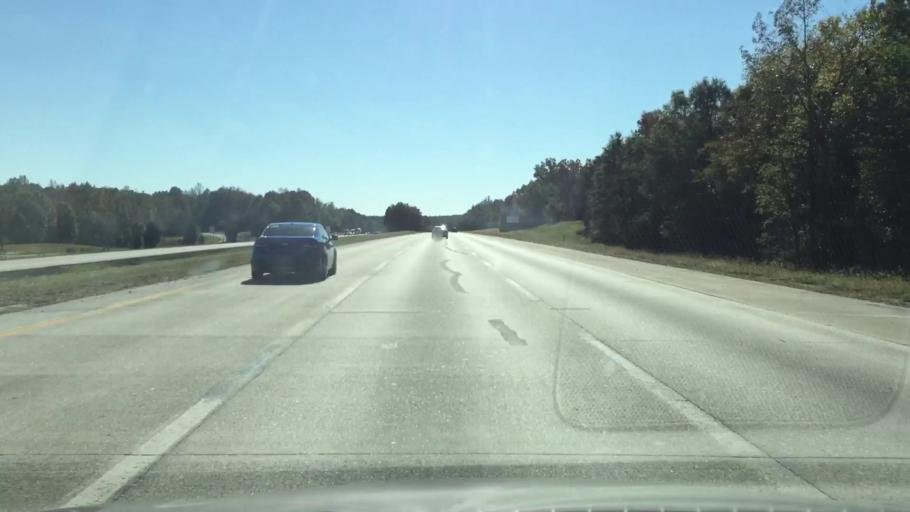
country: US
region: North Carolina
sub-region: Guilford County
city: Jamestown
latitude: 35.9594
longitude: -79.8955
